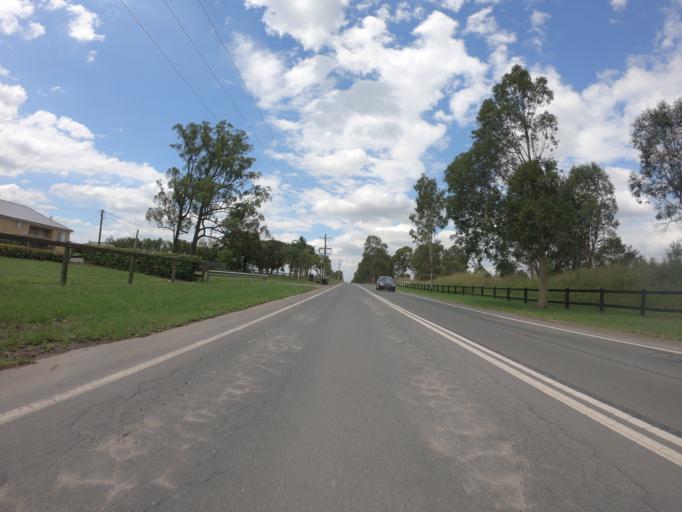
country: AU
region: New South Wales
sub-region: Liverpool
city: Luddenham
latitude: -33.8360
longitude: 150.7517
